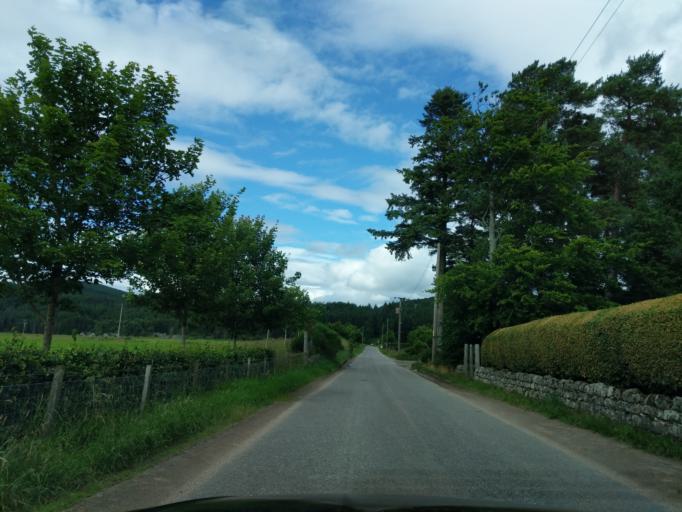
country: GB
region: Scotland
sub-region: Aberdeenshire
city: Ballater
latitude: 57.0410
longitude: -3.0553
